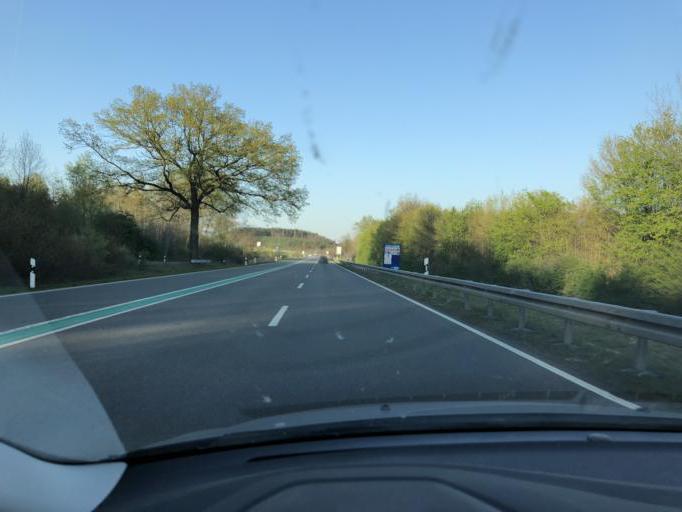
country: DE
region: Brandenburg
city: Schwarzbach
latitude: 51.4866
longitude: 13.9328
